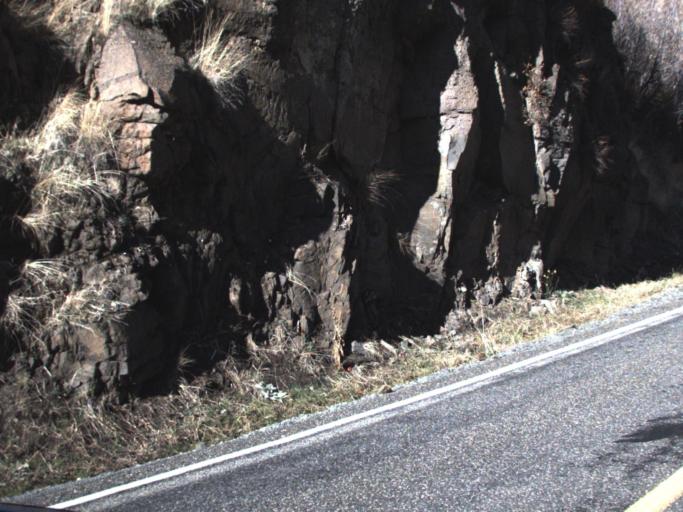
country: US
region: Washington
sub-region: Asotin County
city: Asotin
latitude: 46.0477
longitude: -117.2426
